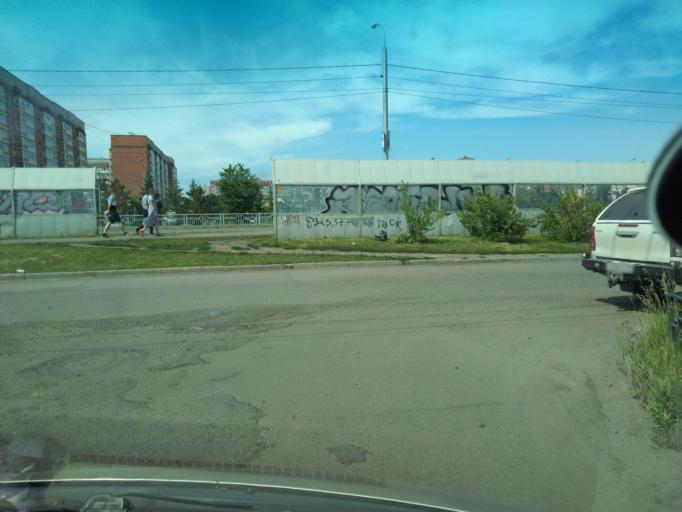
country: RU
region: Krasnoyarskiy
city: Krasnoyarsk
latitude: 56.0520
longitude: 92.9151
